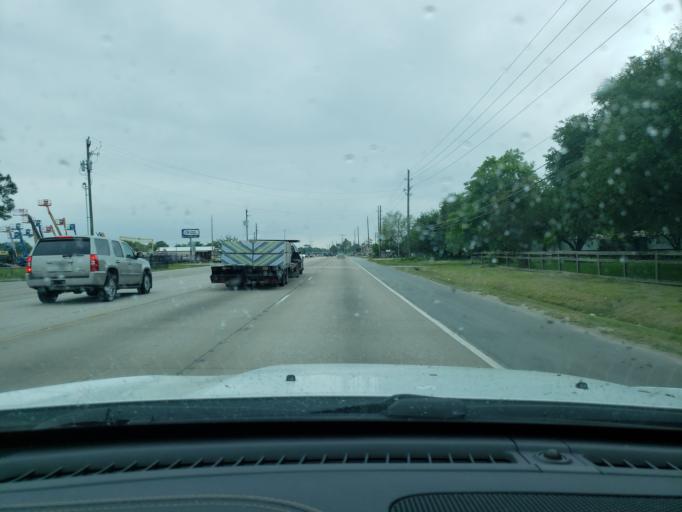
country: US
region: Texas
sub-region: Chambers County
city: Mont Belvieu
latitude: 29.8077
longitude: -94.9032
